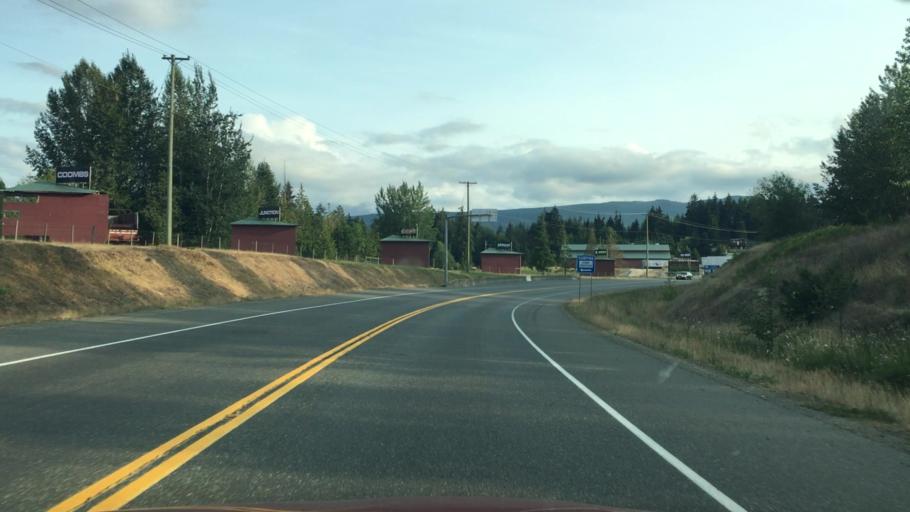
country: CA
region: British Columbia
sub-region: Regional District of Nanaimo
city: Parksville
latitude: 49.3062
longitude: -124.4501
